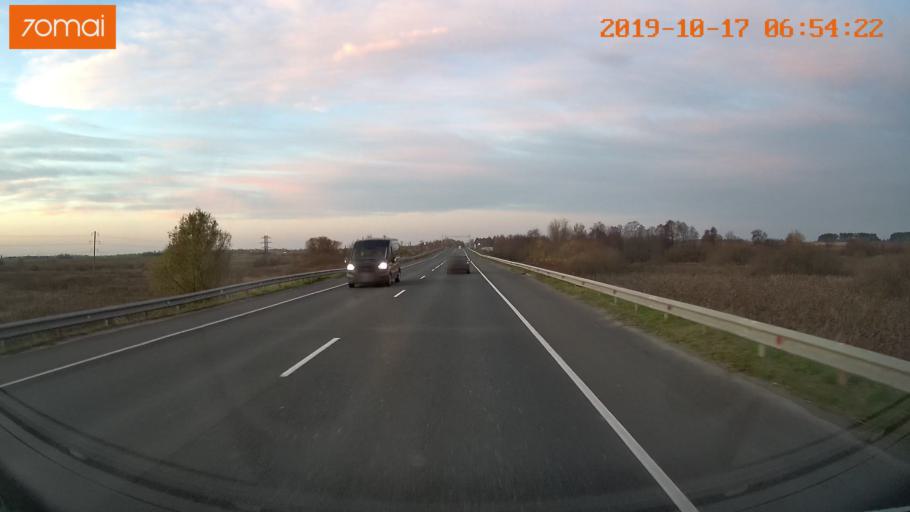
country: RU
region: Vladimir
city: Suzdal'
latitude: 56.4642
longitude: 40.4702
